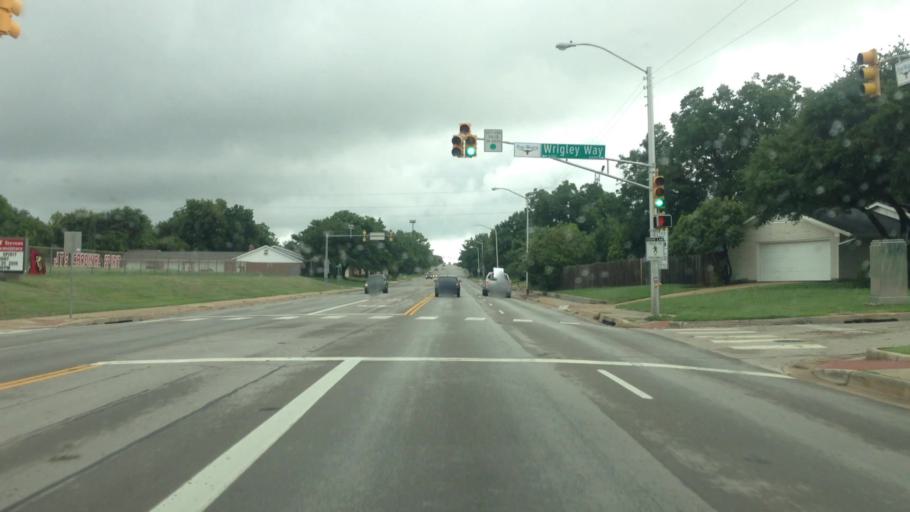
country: US
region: Texas
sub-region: Tarrant County
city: Edgecliff Village
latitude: 32.6551
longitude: -97.3959
